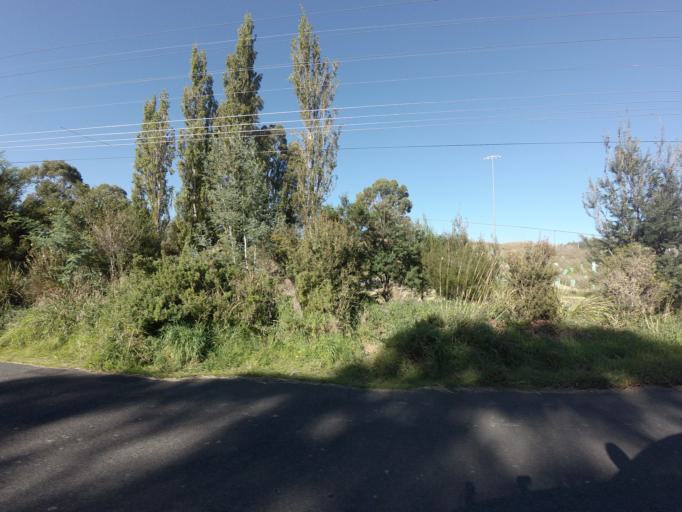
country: AU
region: Tasmania
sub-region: Clarence
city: Lindisfarne
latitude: -42.8350
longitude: 147.3470
